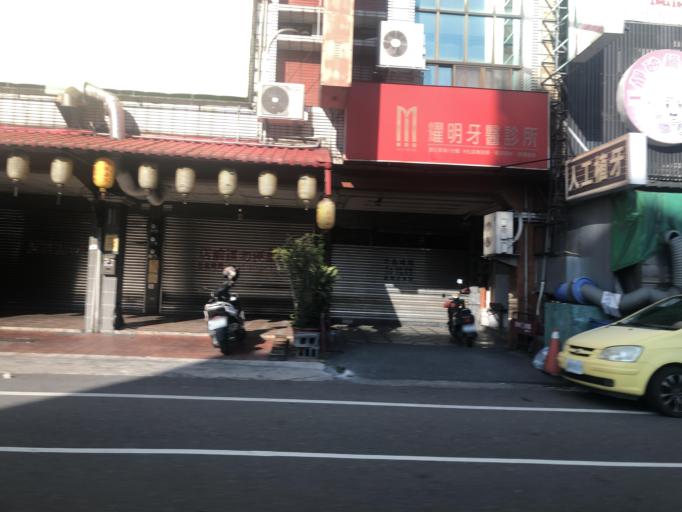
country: TW
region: Taiwan
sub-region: Tainan
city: Tainan
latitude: 23.0121
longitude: 120.2316
